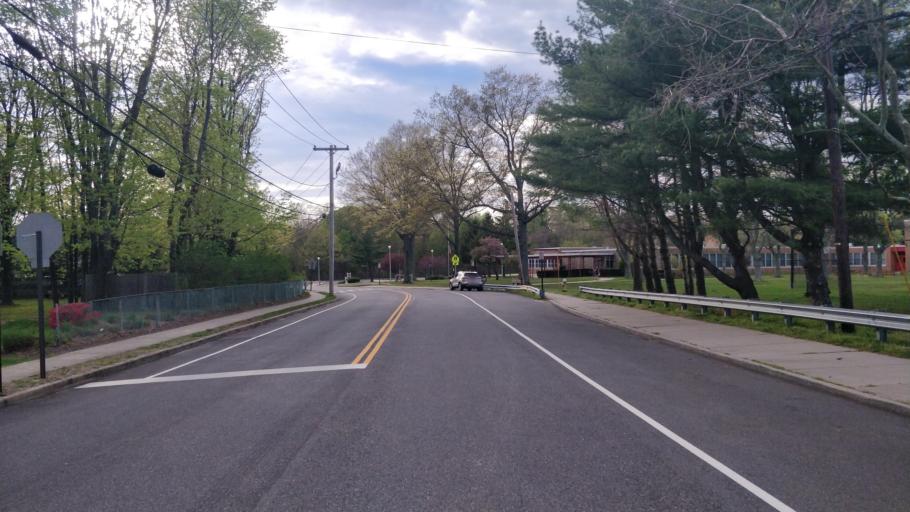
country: US
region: New York
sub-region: Suffolk County
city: Northport
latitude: 40.9125
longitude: -73.3264
